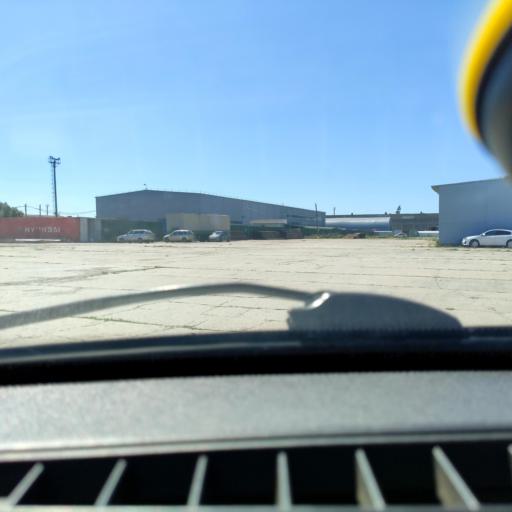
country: RU
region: Samara
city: Tol'yatti
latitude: 53.5735
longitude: 49.3023
